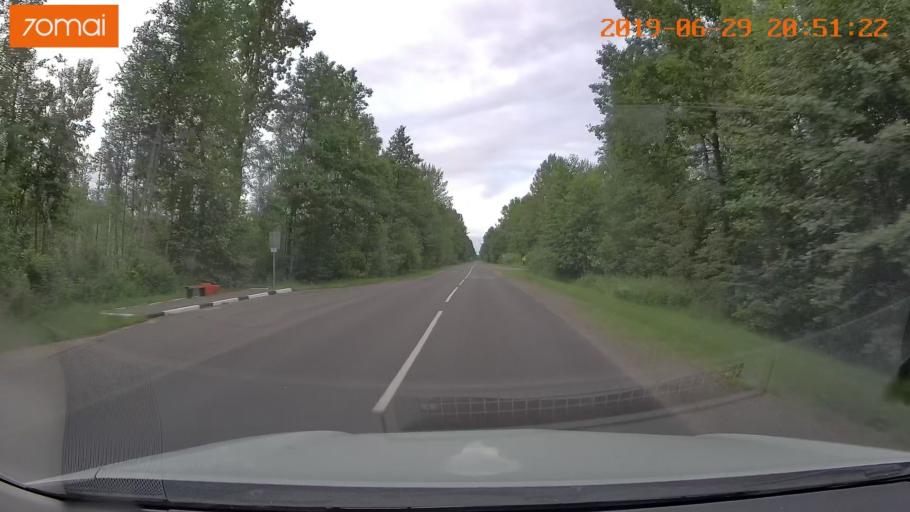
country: BY
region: Brest
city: Hantsavichy
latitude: 52.6872
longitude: 26.3484
